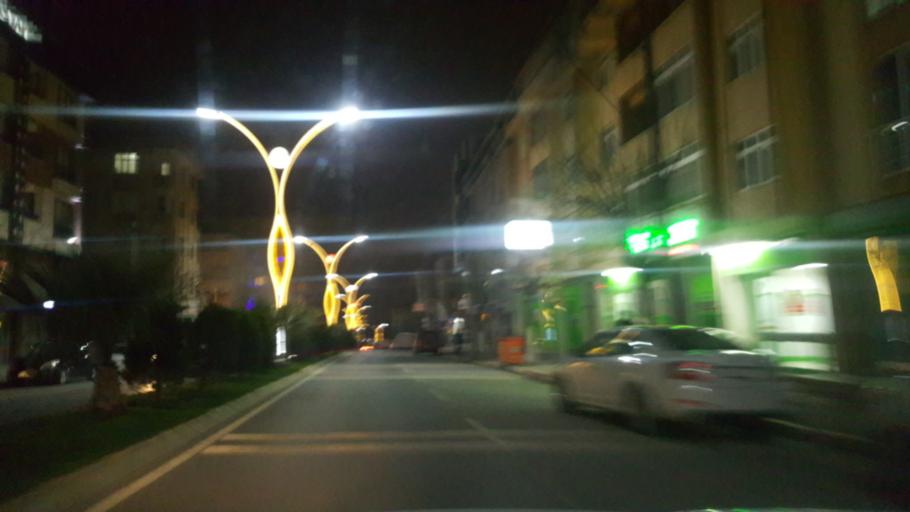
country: TR
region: Kocaeli
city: Darica
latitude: 40.7787
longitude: 29.4030
